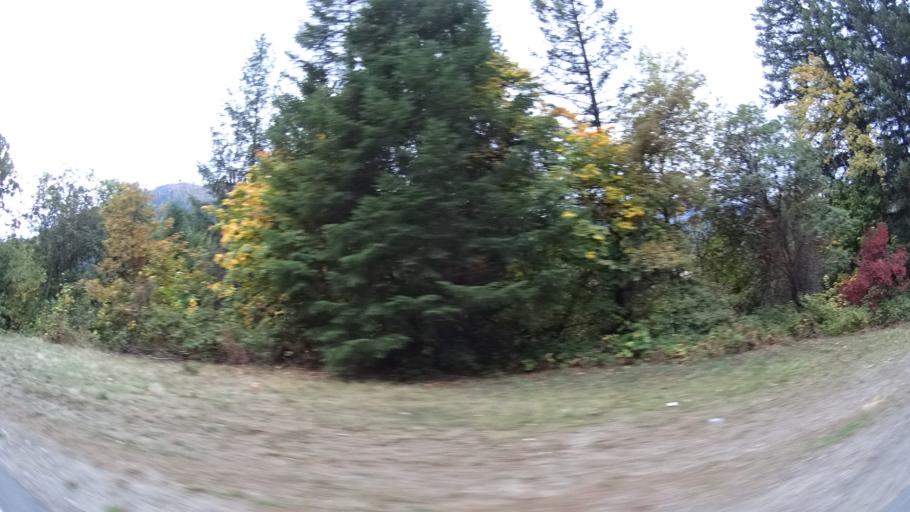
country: US
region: California
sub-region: Siskiyou County
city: Happy Camp
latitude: 41.8047
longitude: -123.3461
